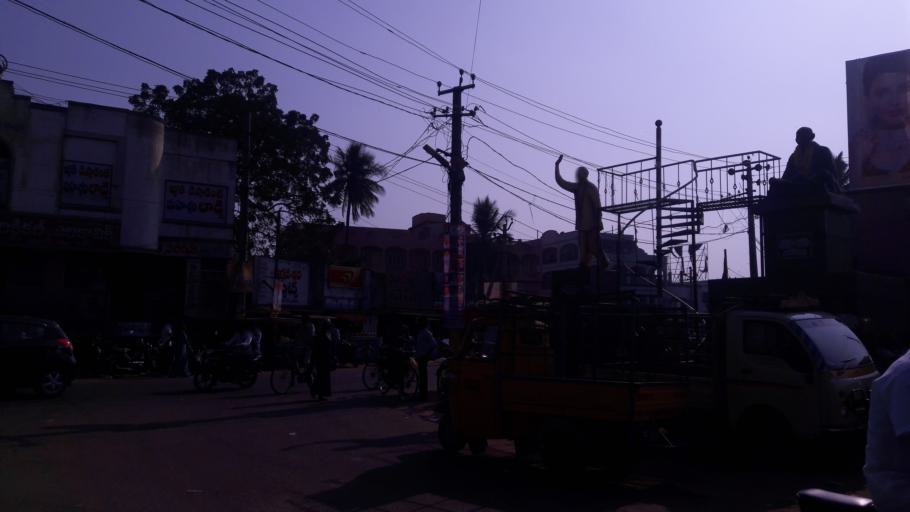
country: IN
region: Andhra Pradesh
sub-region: West Godavari
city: Akividu
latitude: 16.5811
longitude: 81.3731
